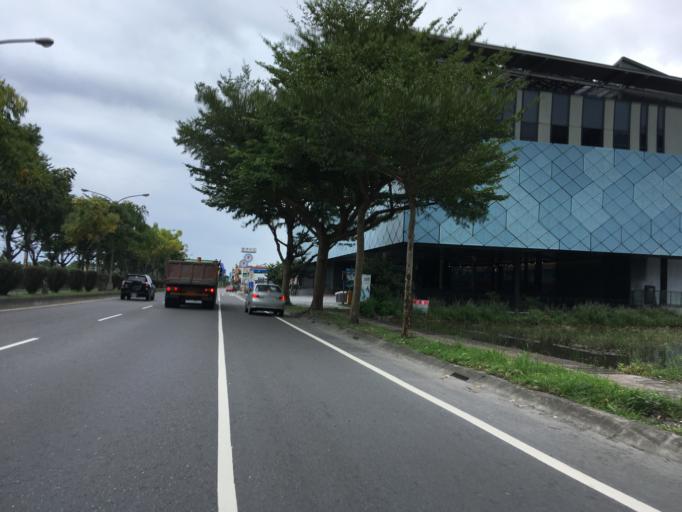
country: TW
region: Taiwan
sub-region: Yilan
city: Yilan
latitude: 24.6149
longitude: 121.8172
